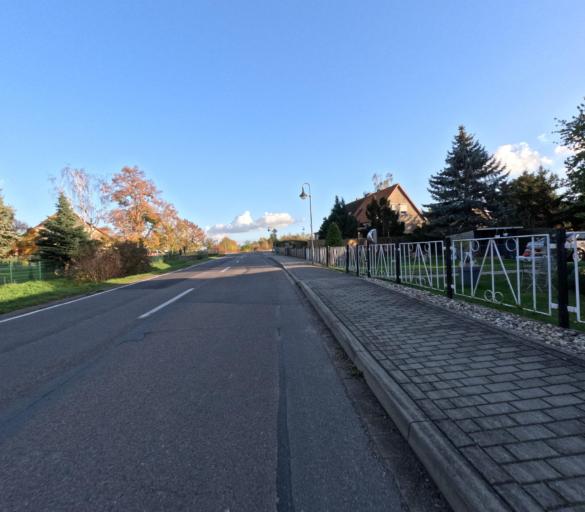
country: DE
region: Saxony-Anhalt
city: Gunthersdorf
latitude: 51.3538
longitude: 12.1700
